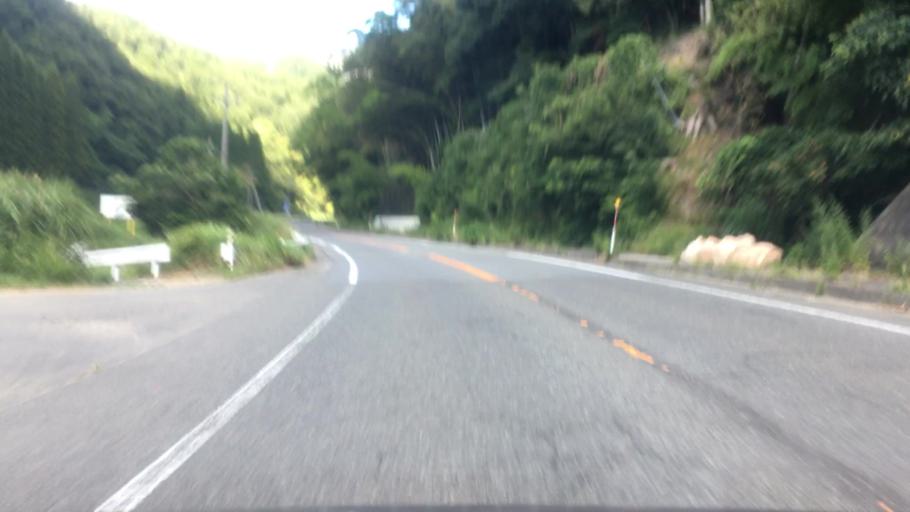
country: JP
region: Hyogo
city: Toyooka
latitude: 35.5762
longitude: 134.7603
